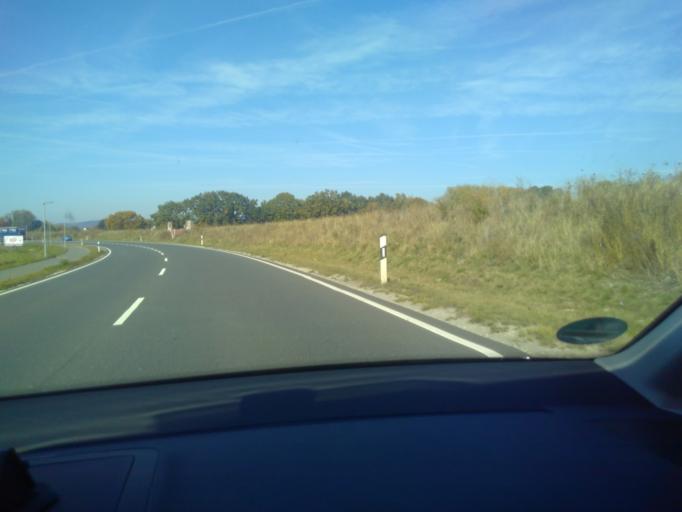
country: DE
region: North Rhine-Westphalia
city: Halle
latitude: 52.0299
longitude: 8.3795
